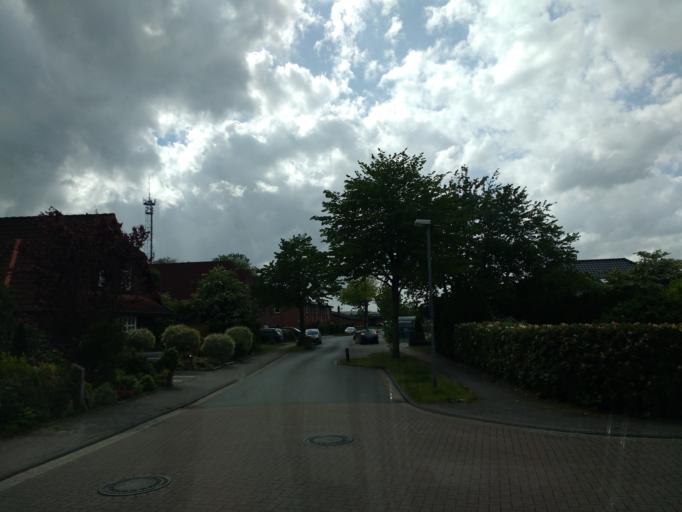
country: DE
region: Lower Saxony
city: Jever
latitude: 53.5806
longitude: 7.9112
